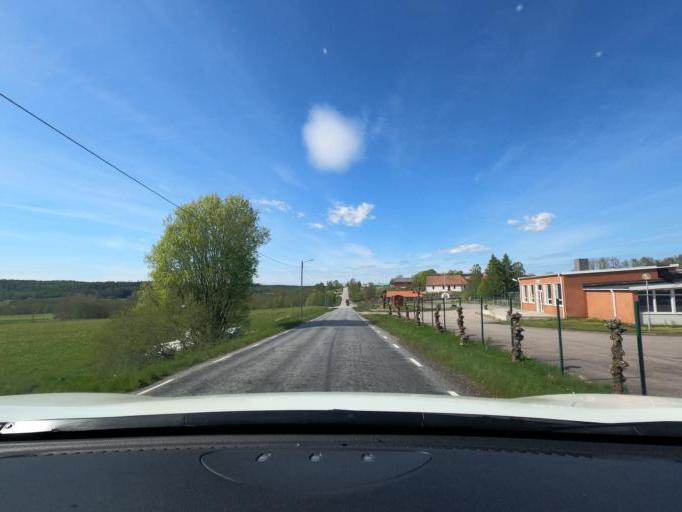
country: SE
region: Vaestra Goetaland
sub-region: Marks Kommun
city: Bua
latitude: 57.5021
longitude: 12.5513
